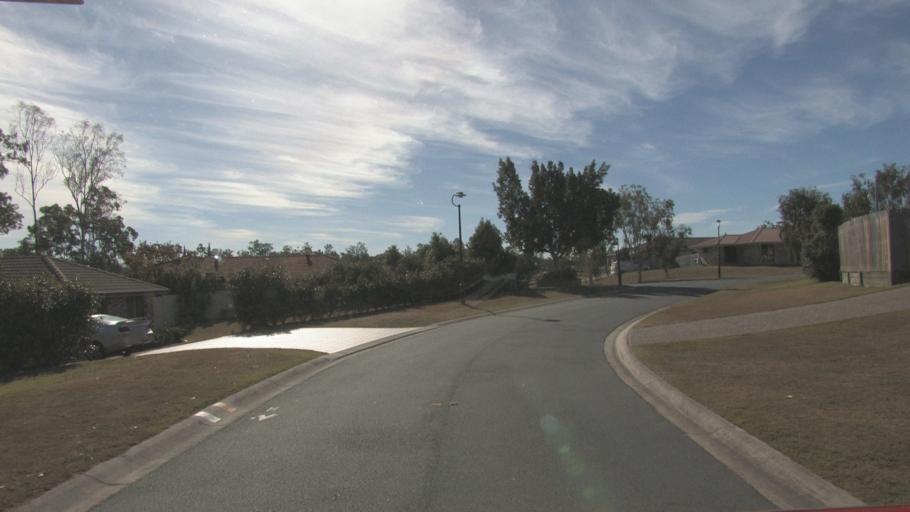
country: AU
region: Queensland
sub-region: Logan
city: North Maclean
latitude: -27.8108
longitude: 152.9504
